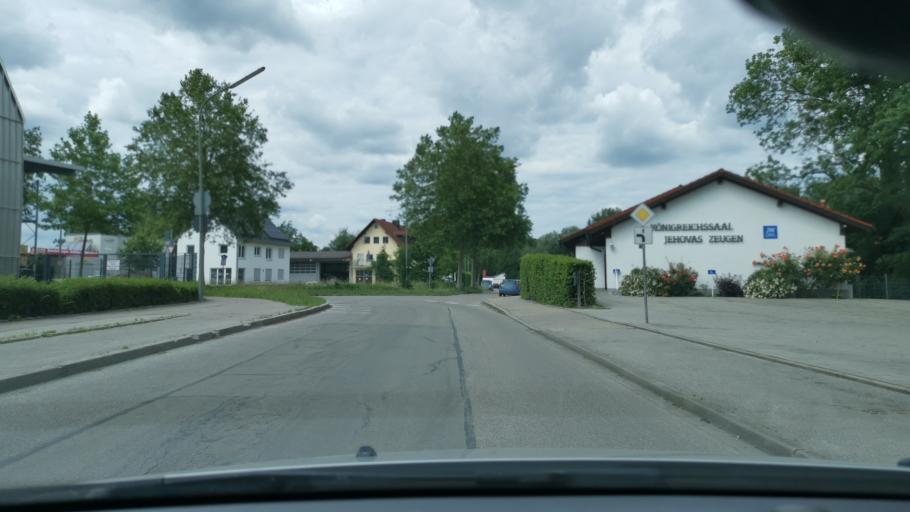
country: DE
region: Bavaria
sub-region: Upper Bavaria
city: Moosburg
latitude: 48.4738
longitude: 11.9463
